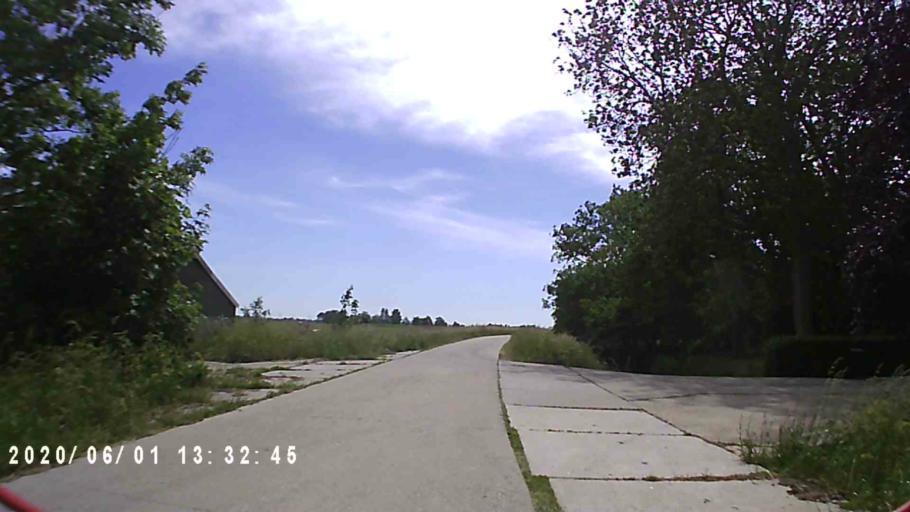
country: NL
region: Friesland
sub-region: Gemeente Littenseradiel
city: Wommels
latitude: 53.0925
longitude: 5.5686
